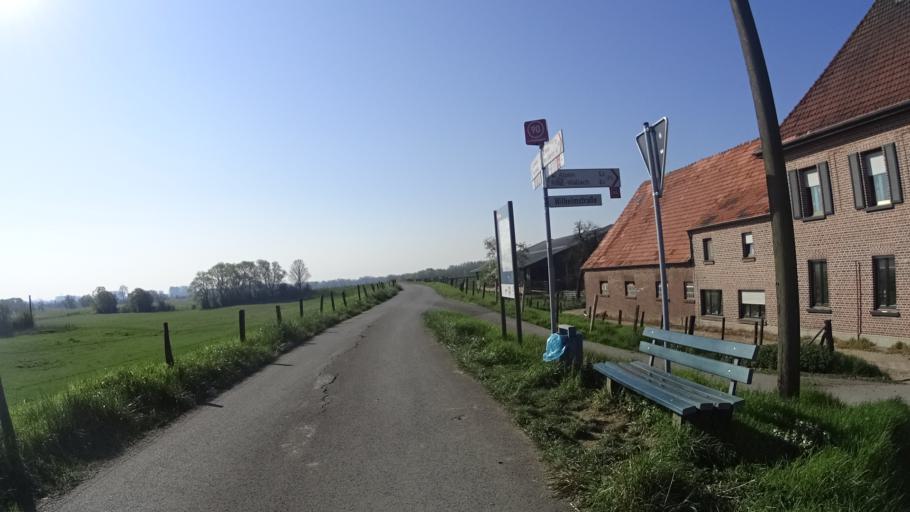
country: DE
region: North Rhine-Westphalia
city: Rheinberg
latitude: 51.5952
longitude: 6.5850
